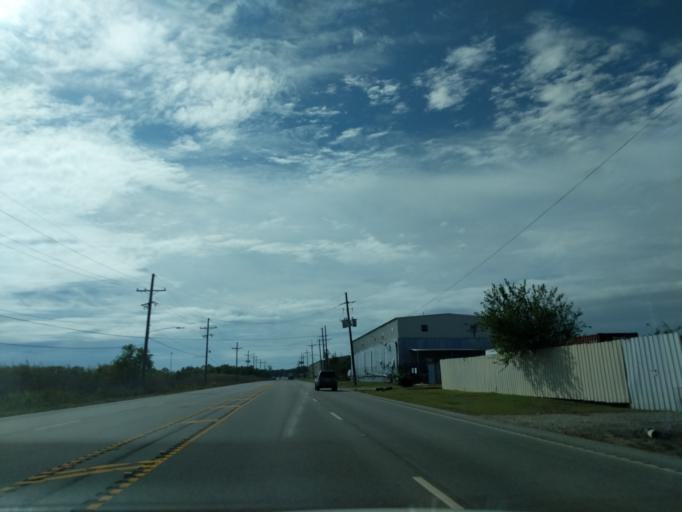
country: US
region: Louisiana
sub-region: Saint Tammany Parish
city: Eden Isle
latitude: 30.0768
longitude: -89.8486
